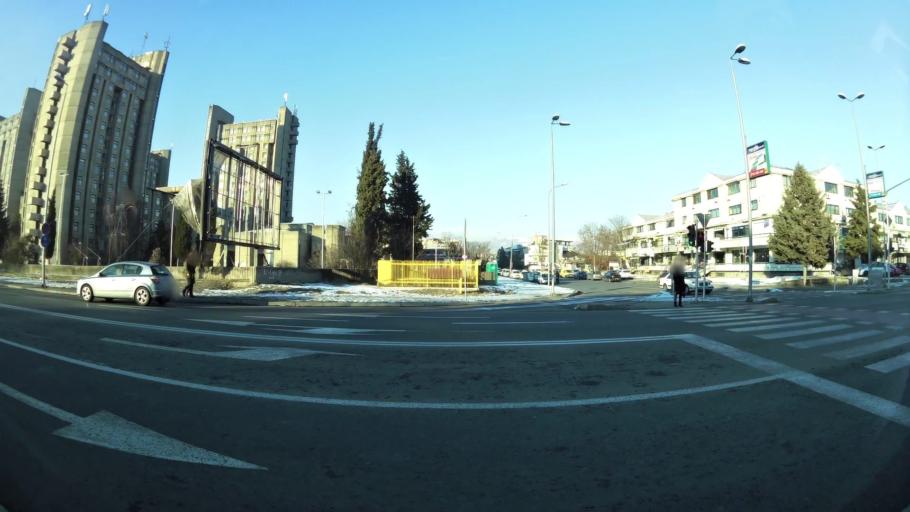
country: MK
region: Karpos
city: Skopje
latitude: 41.9981
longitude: 21.3911
